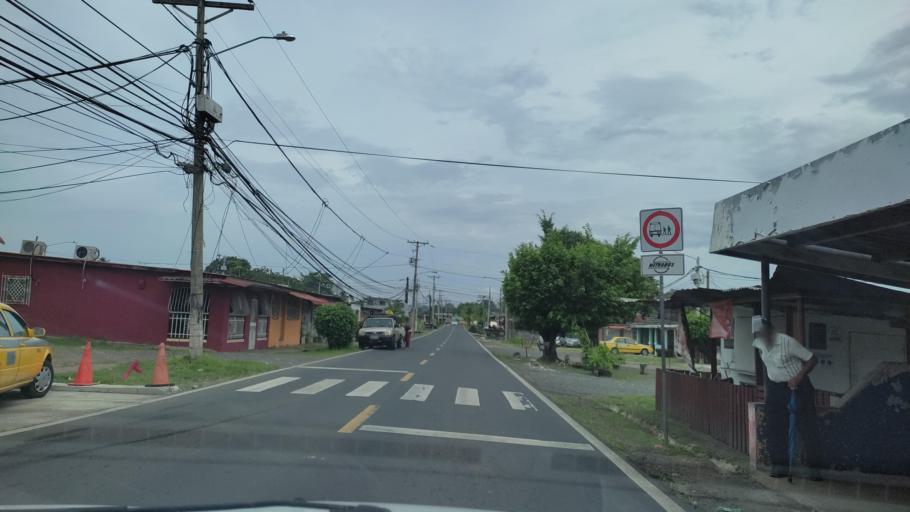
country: PA
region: Panama
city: San Miguelito
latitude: 9.0485
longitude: -79.4318
